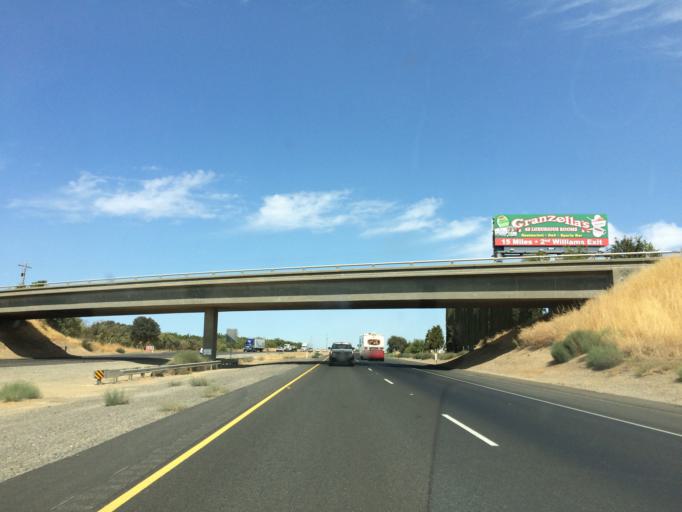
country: US
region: California
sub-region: Colusa County
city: Arbuckle
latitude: 38.9654
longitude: -122.0254
